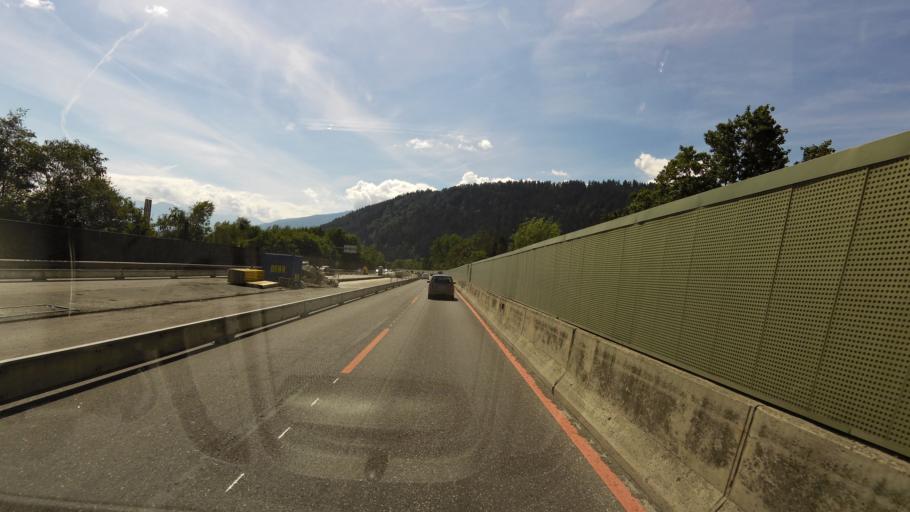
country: AT
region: Tyrol
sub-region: Politischer Bezirk Innsbruck Land
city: Zirl
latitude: 47.2679
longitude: 11.2307
